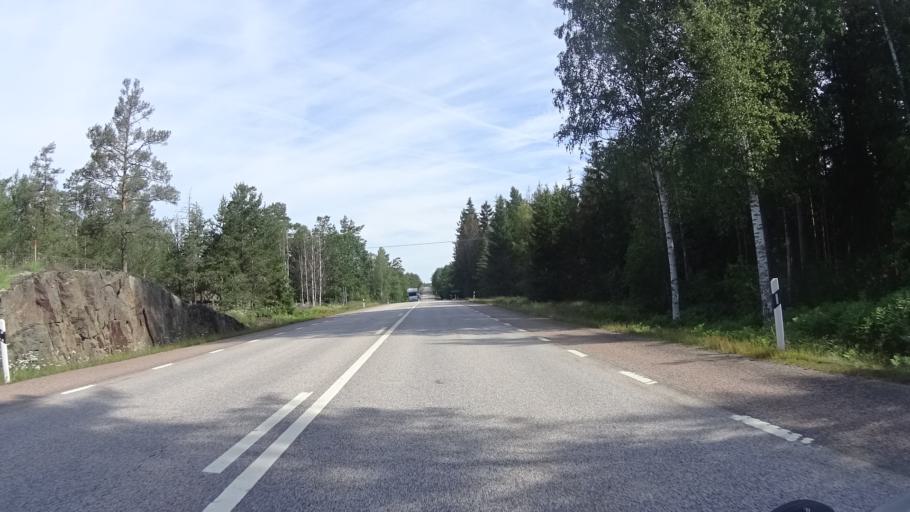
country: SE
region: Kalmar
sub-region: Oskarshamns Kommun
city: Oskarshamn
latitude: 57.4738
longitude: 16.5175
